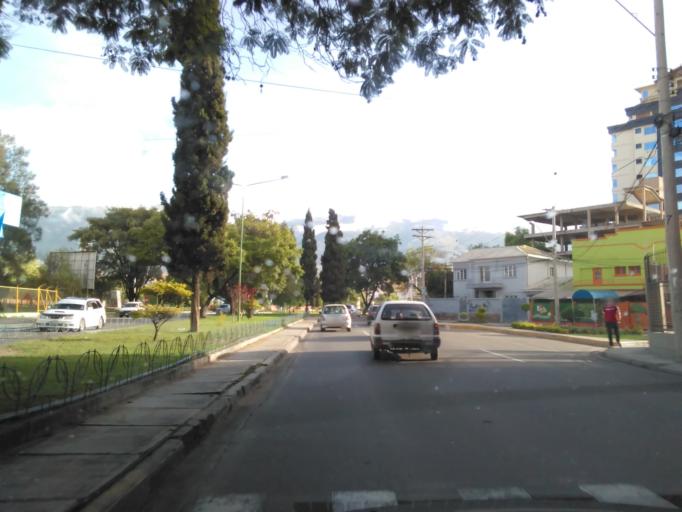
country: BO
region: Cochabamba
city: Cochabamba
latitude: -17.3836
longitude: -66.1620
